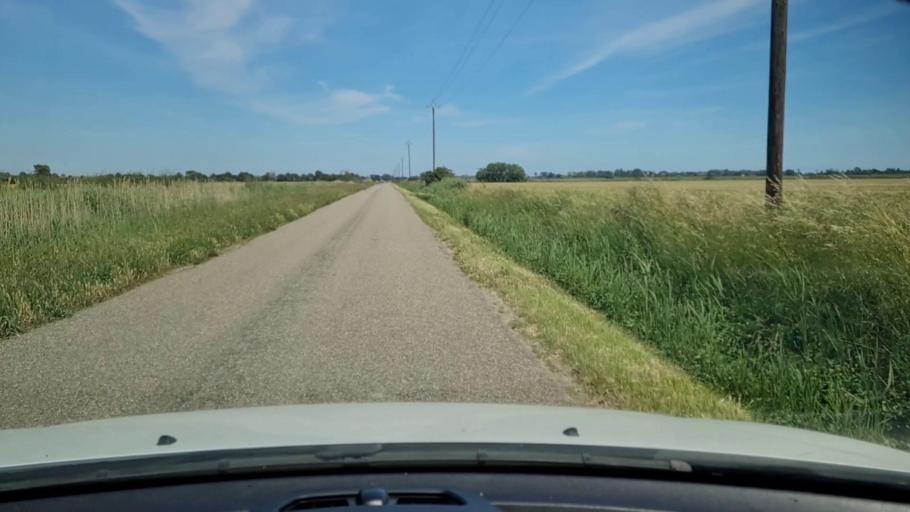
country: FR
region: Languedoc-Roussillon
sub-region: Departement du Gard
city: Saint-Gilles
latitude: 43.6028
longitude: 4.4411
